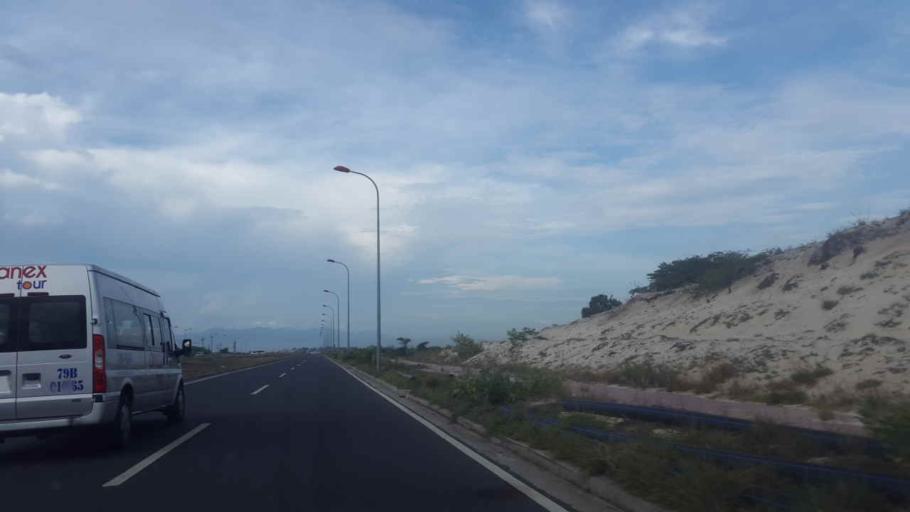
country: VN
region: Khanh Hoa
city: Cam Lam
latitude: 12.0088
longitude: 109.2105
